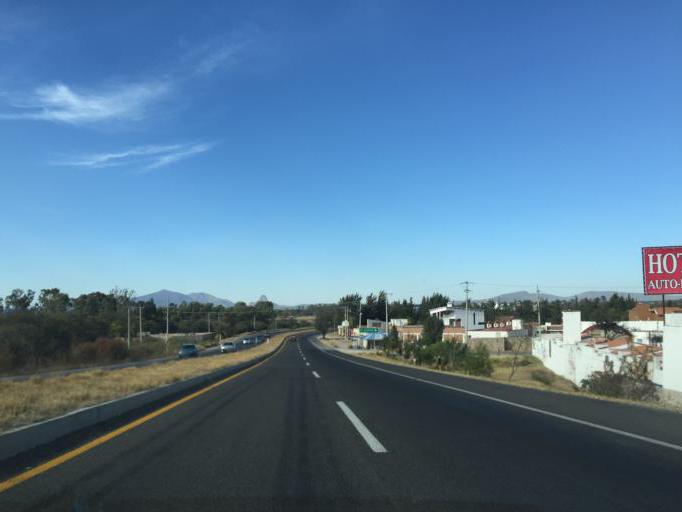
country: MX
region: Queretaro
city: Ezequiel Montes
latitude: 20.6138
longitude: -99.9143
